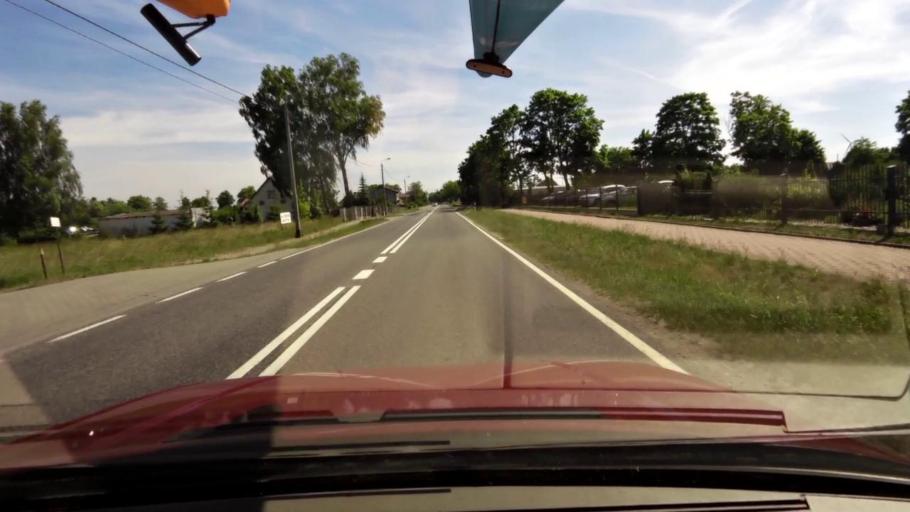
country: PL
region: Pomeranian Voivodeship
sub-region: Powiat slupski
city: Kobylnica
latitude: 54.4134
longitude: 17.0077
